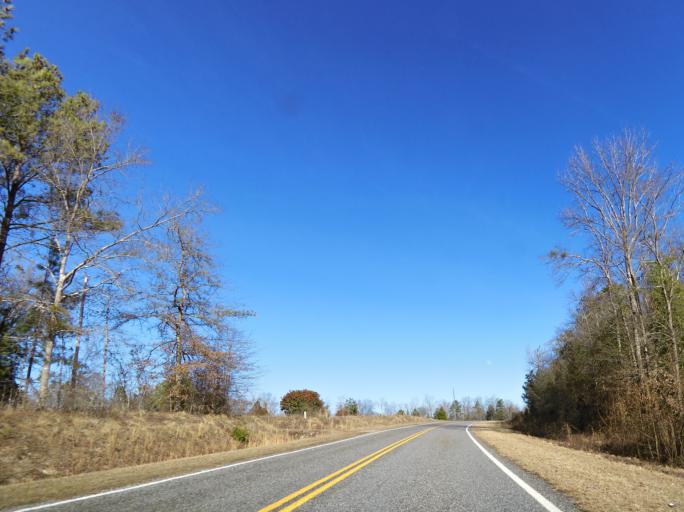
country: US
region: Georgia
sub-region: Crawford County
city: Knoxville
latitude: 32.7255
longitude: -83.9840
